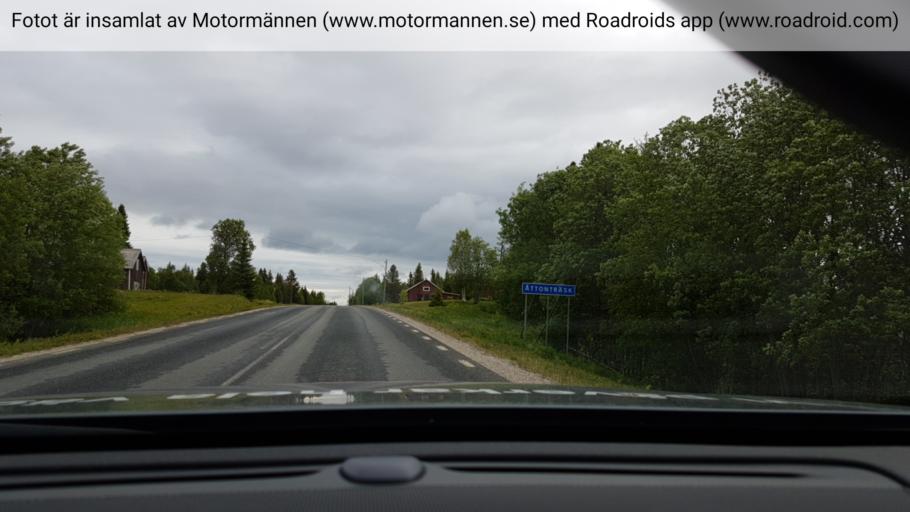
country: SE
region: Vaesterbotten
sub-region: Lycksele Kommun
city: Soderfors
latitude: 64.4235
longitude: 18.0565
